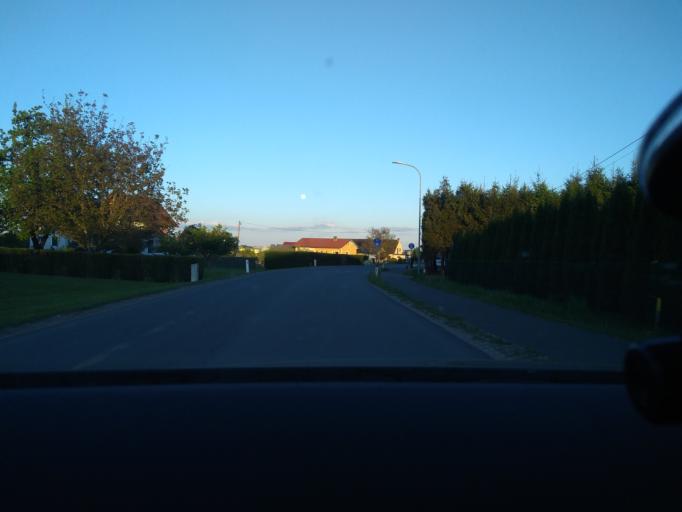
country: AT
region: Styria
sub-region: Politischer Bezirk Deutschlandsberg
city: Lannach
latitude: 46.9597
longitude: 15.3189
